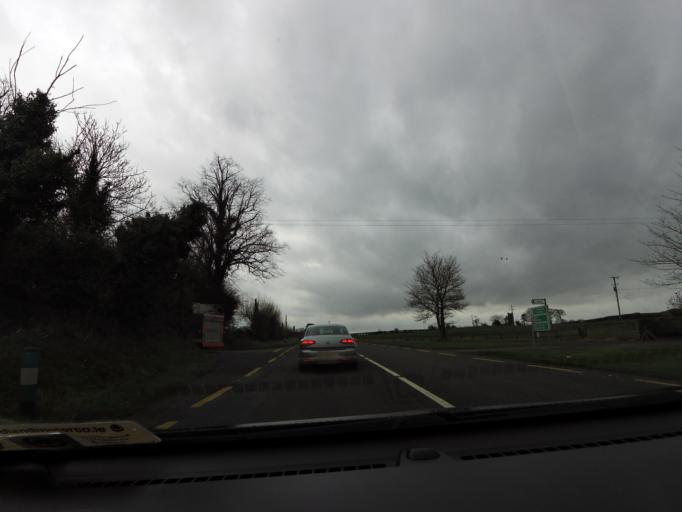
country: IE
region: Leinster
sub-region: Kilkenny
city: Ballyragget
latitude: 52.7329
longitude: -7.3158
